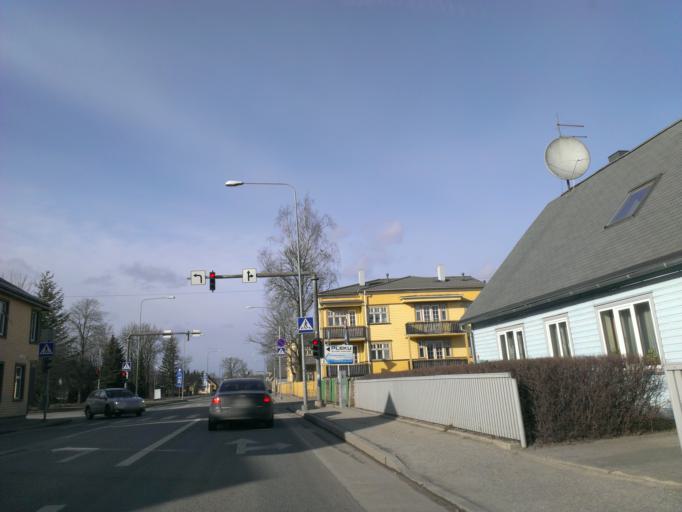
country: EE
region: Paernumaa
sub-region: Paernu linn
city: Parnu
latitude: 58.3974
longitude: 24.4939
